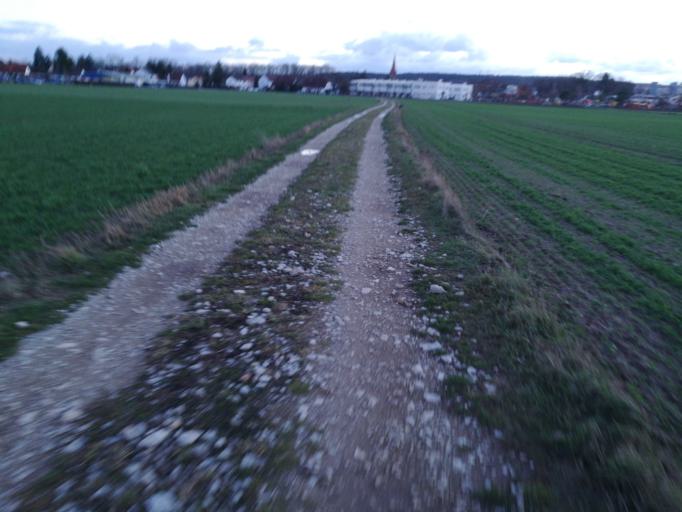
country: DE
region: Bavaria
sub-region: Regierungsbezirk Mittelfranken
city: Obermichelbach
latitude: 49.4952
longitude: 10.9259
